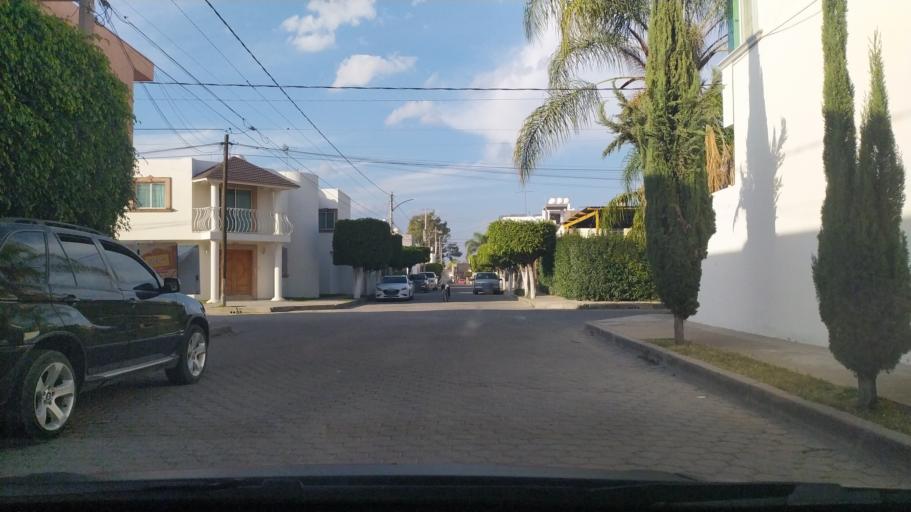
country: MX
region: Guanajuato
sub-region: Purisima del Rincon
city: Monte Grande
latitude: 21.0070
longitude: -101.8613
